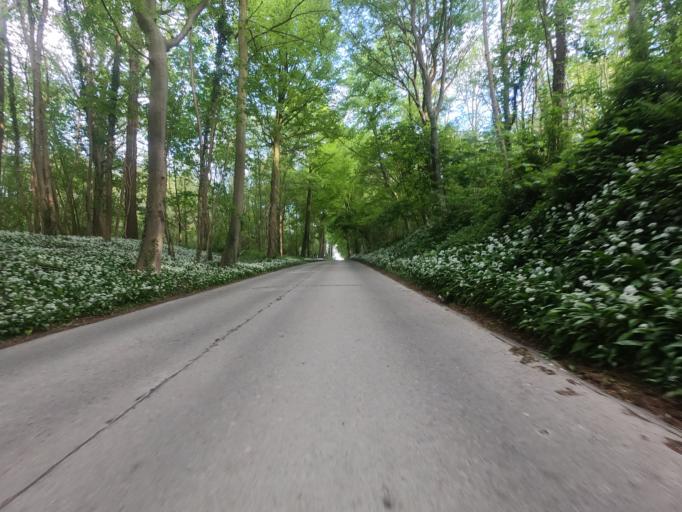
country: BE
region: Flanders
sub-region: Provincie Vlaams-Brabant
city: Galmaarden
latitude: 50.7918
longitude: 3.9797
